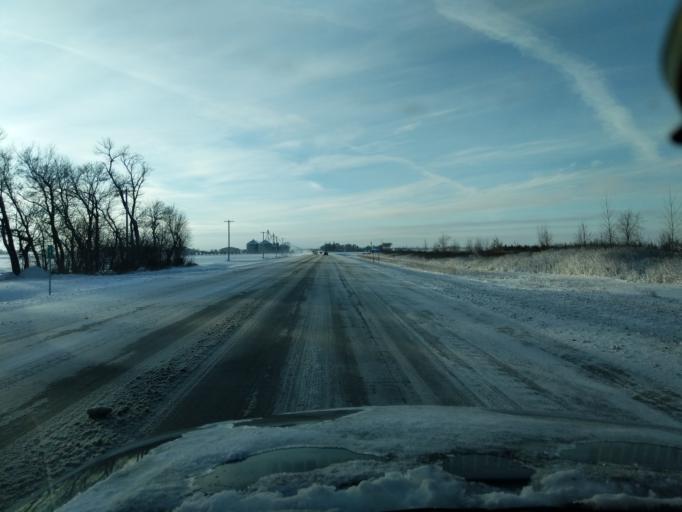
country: US
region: Minnesota
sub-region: Renville County
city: Bird Island
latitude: 44.7675
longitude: -94.9111
